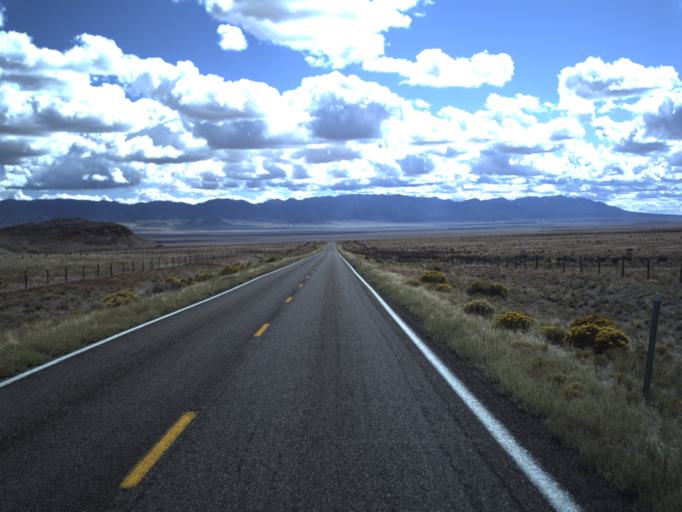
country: US
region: Utah
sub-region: Beaver County
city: Milford
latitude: 38.5954
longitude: -113.8252
